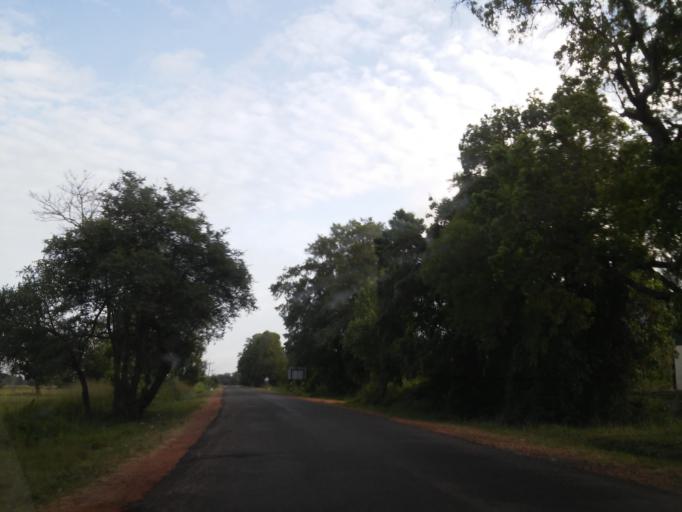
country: LK
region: Central
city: Sigiriya
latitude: 8.0901
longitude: 80.6376
